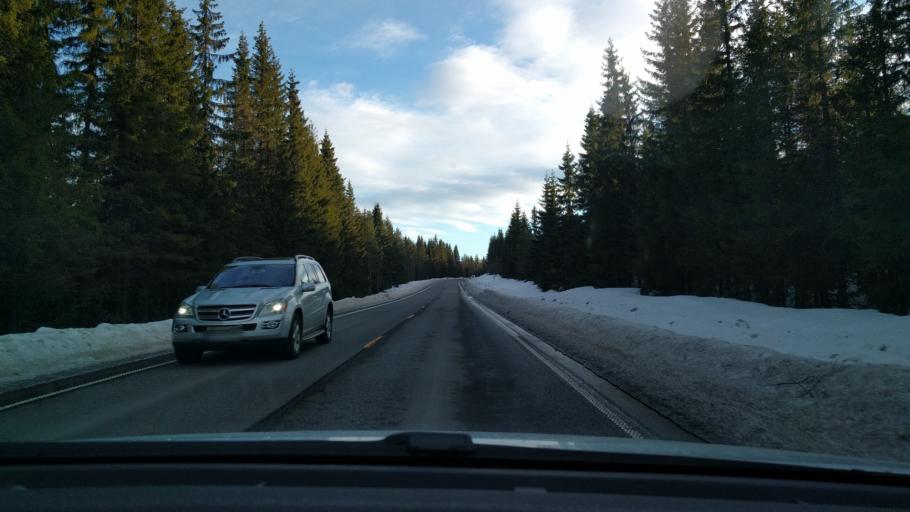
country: NO
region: Hedmark
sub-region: Trysil
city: Innbygda
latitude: 61.0678
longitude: 11.9708
